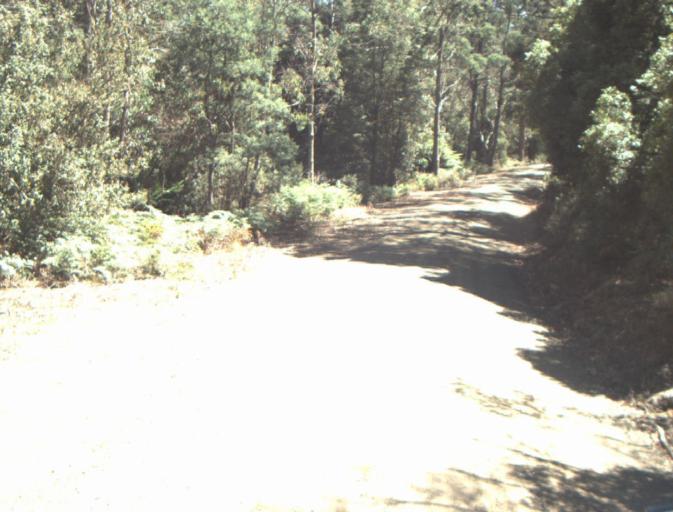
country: AU
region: Tasmania
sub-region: Dorset
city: Scottsdale
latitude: -41.3585
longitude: 147.4269
